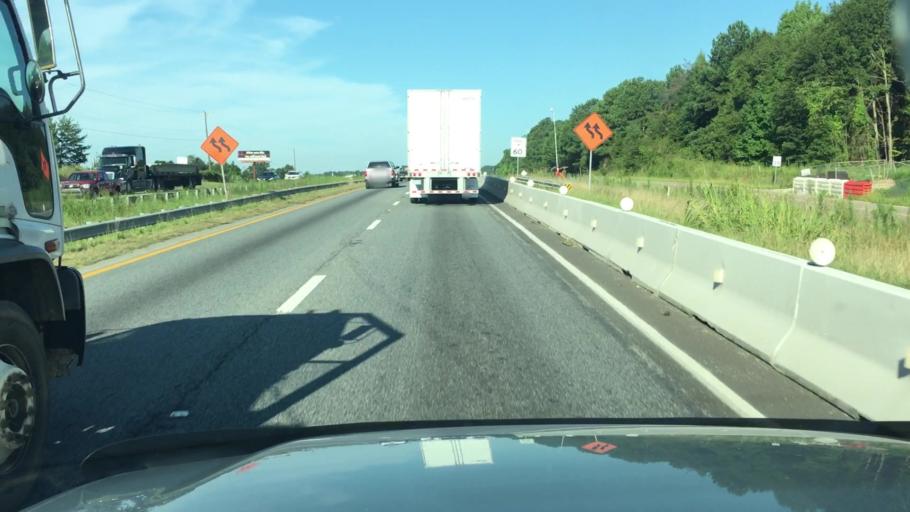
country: US
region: South Carolina
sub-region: Spartanburg County
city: Mayo
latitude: 35.0296
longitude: -81.8628
